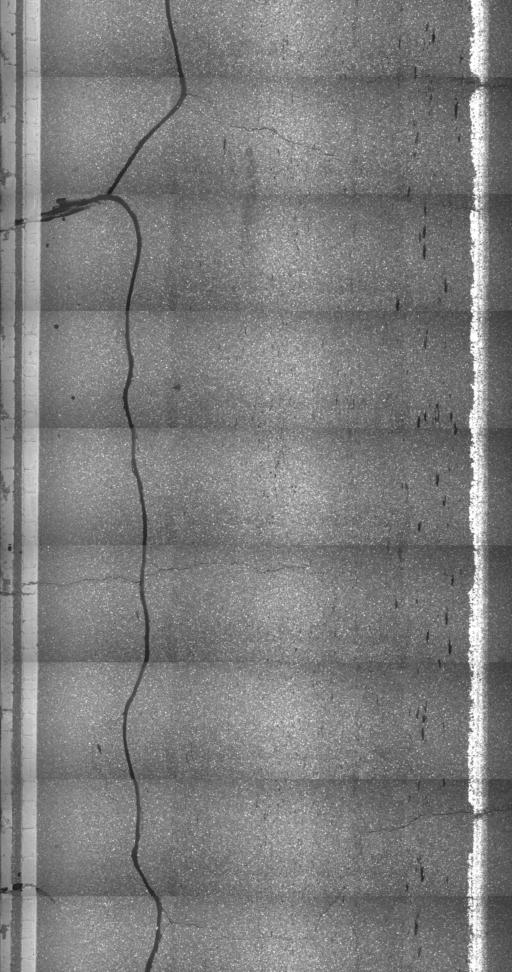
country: US
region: Vermont
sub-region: Windsor County
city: Springfield
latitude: 43.3196
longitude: -72.5055
